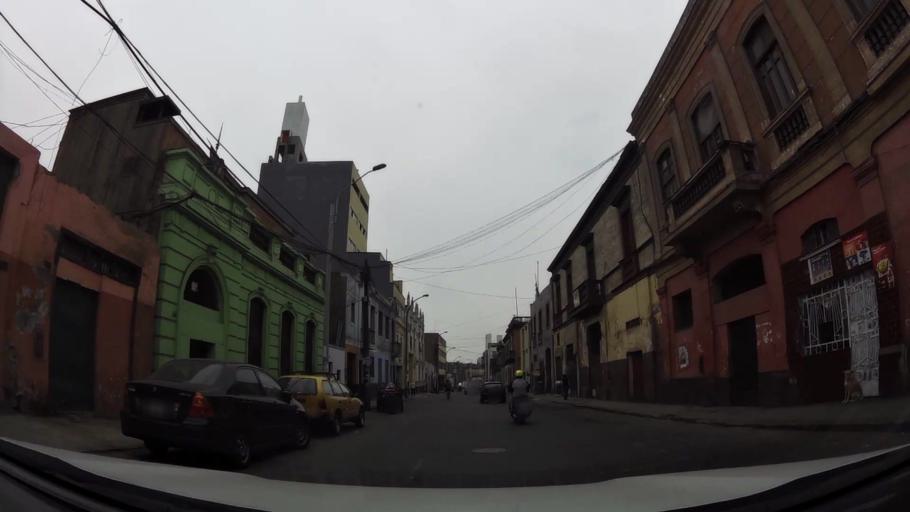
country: PE
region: Lima
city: Lima
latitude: -12.0511
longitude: -77.0199
